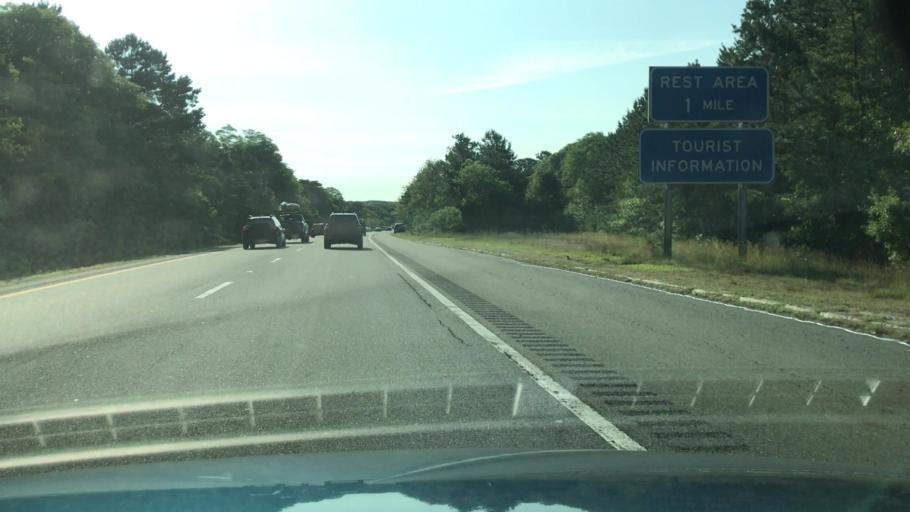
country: US
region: Massachusetts
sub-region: Barnstable County
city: Barnstable
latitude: 41.6894
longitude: -70.3143
